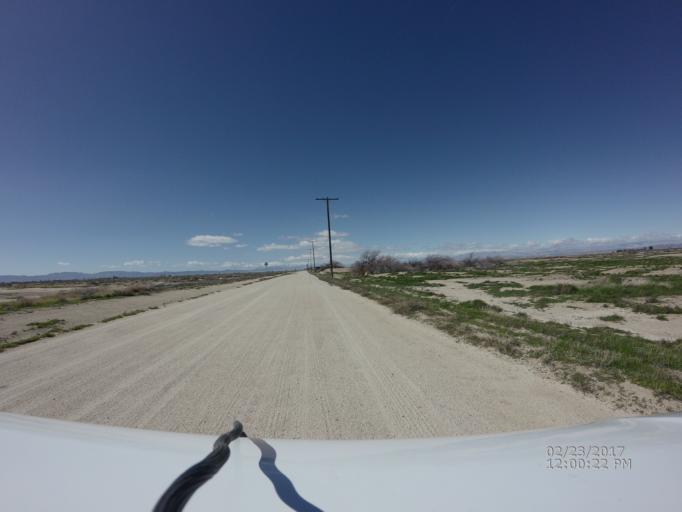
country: US
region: California
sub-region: Los Angeles County
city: Lancaster
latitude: 34.7416
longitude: -117.9704
